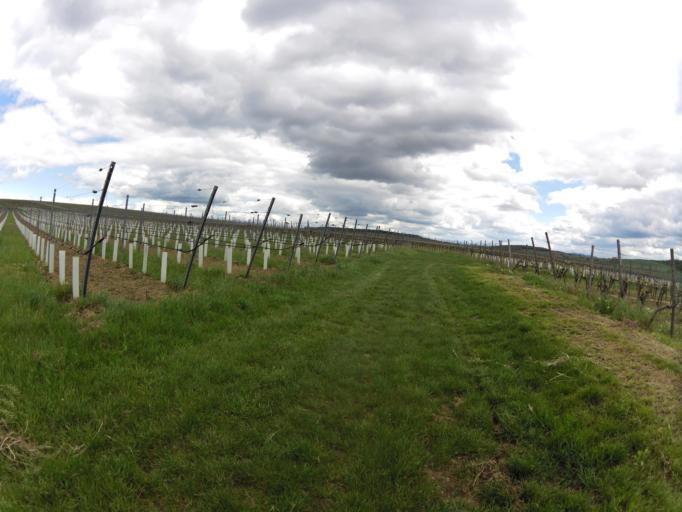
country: DE
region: Bavaria
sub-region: Regierungsbezirk Unterfranken
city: Volkach
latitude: 49.8724
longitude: 10.2381
